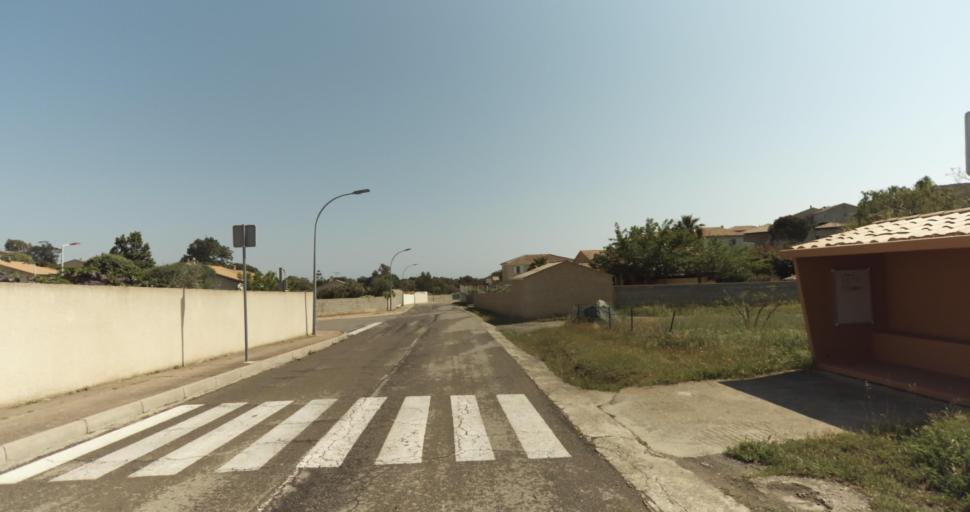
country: FR
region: Corsica
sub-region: Departement de la Haute-Corse
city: Biguglia
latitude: 42.6190
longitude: 9.4250
